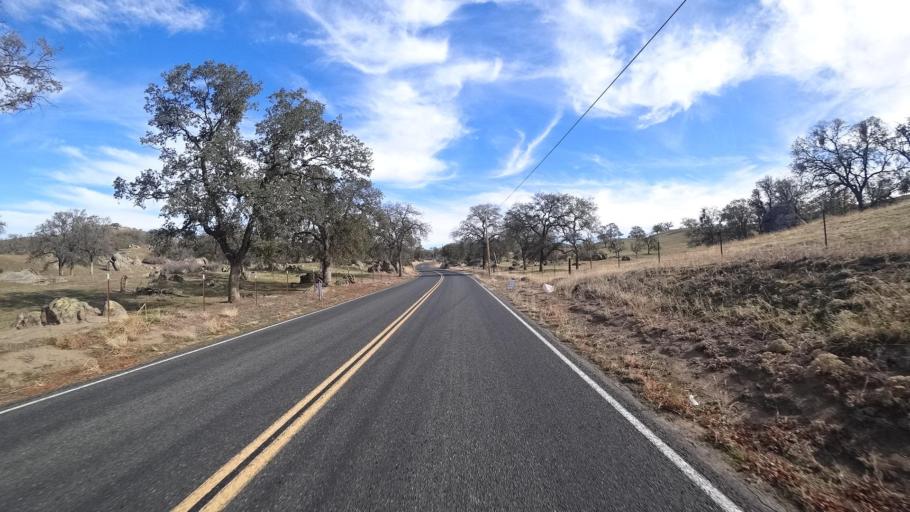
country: US
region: California
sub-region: Kern County
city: Oildale
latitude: 35.6261
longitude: -118.8412
